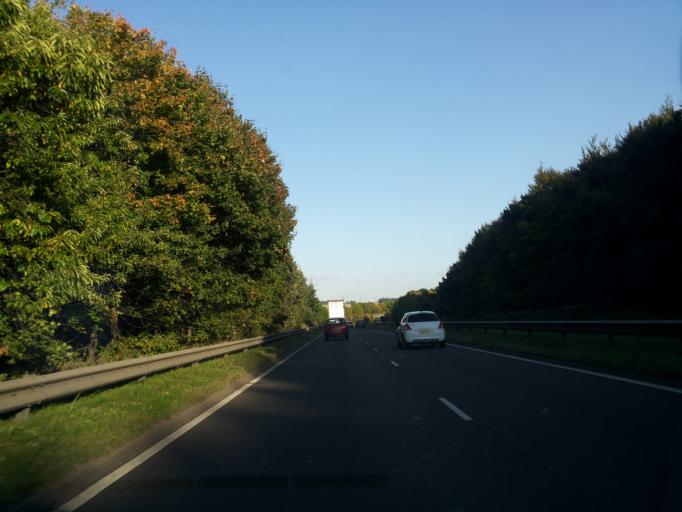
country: GB
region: England
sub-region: Derbyshire
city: Bolsover
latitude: 53.2008
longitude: -1.3381
